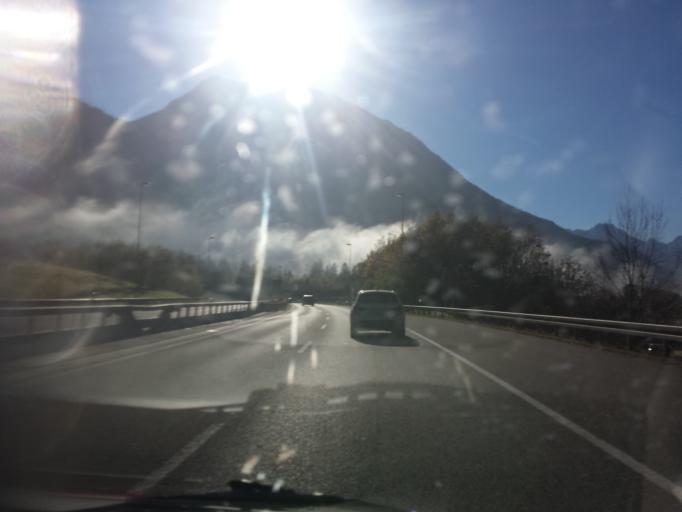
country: DE
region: Bavaria
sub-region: Upper Bavaria
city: Farchant
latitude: 47.5361
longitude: 11.1184
